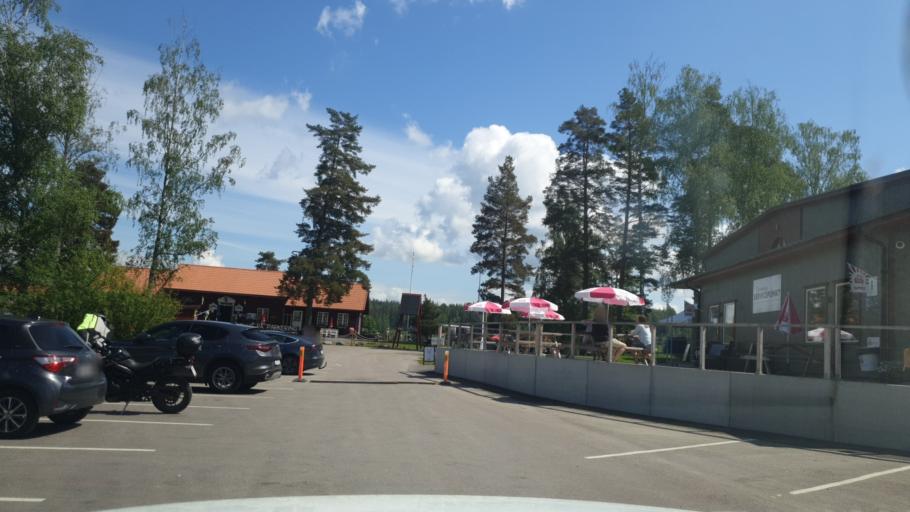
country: SE
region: Vaermland
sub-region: Grums Kommun
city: Slottsbron
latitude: 59.4525
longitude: 12.9114
